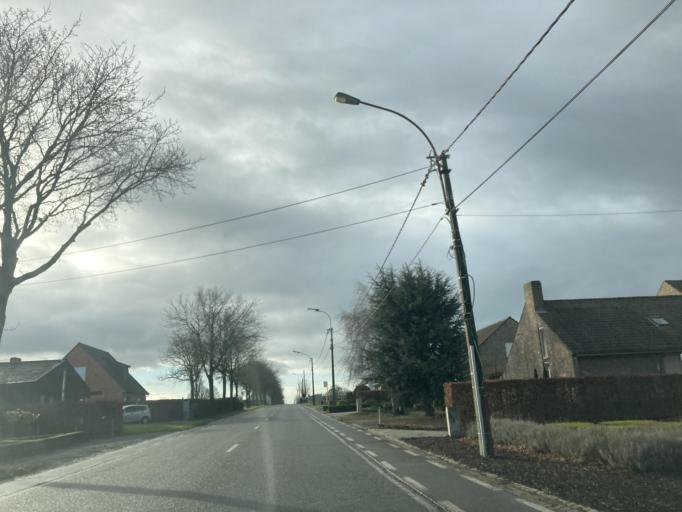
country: BE
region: Flanders
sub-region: Provincie West-Vlaanderen
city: Tielt
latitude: 51.0204
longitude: 3.3326
